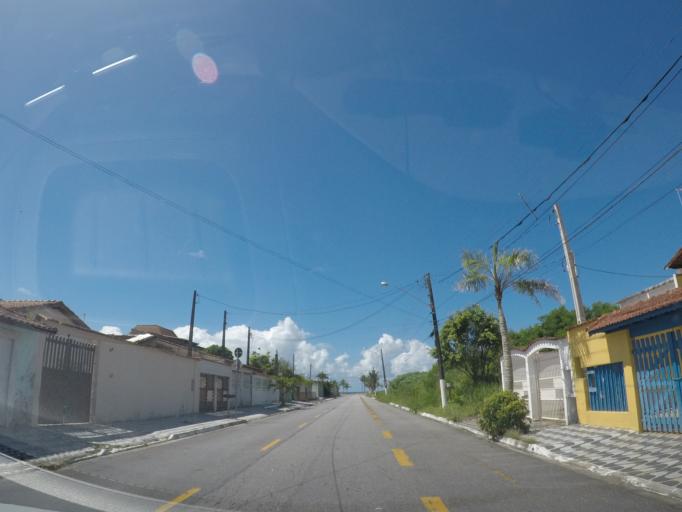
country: BR
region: Sao Paulo
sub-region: Mongagua
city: Mongagua
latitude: -24.0827
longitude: -46.5965
